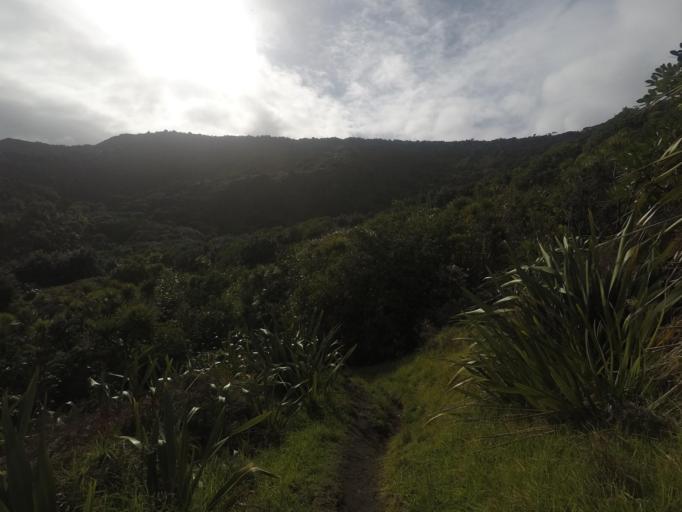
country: NZ
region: Auckland
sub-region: Auckland
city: Muriwai Beach
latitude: -36.8849
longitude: 174.4402
